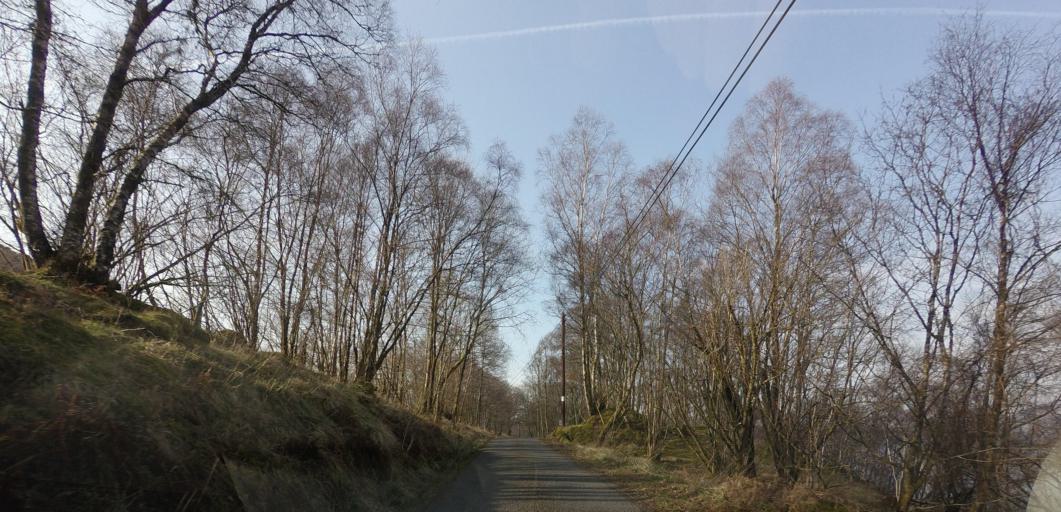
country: GB
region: Scotland
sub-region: Stirling
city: Callander
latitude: 56.4763
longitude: -4.2637
